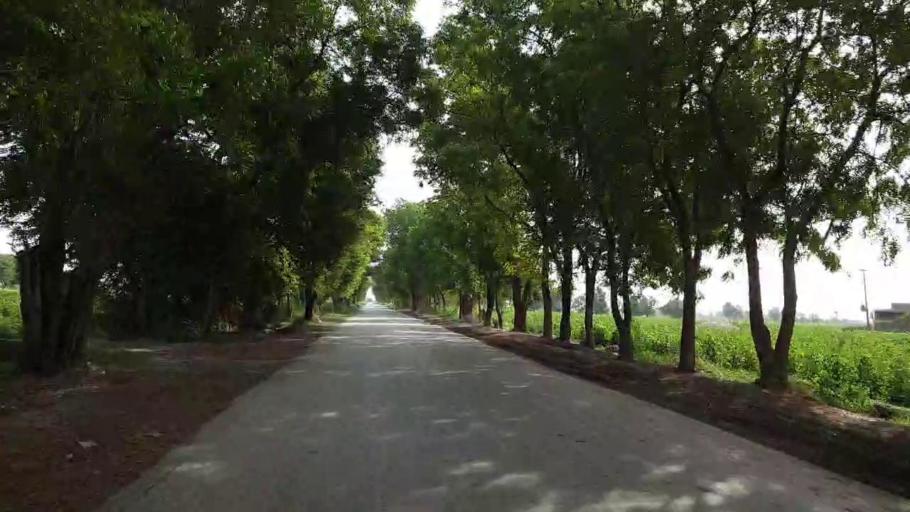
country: PK
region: Sindh
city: Nawabshah
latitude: 26.2523
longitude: 68.4634
